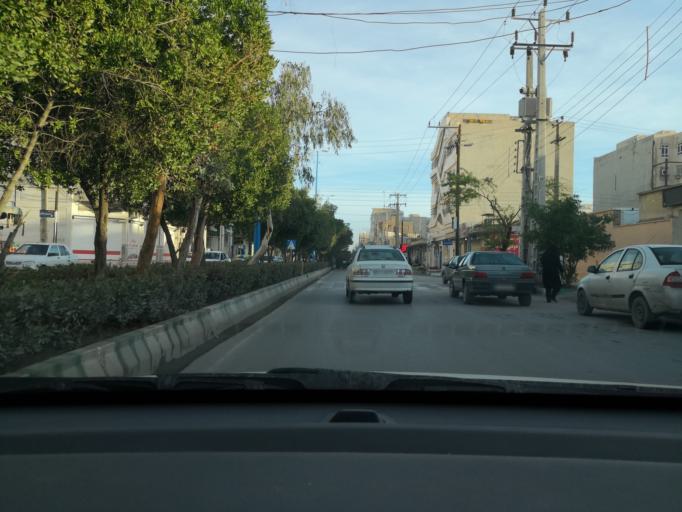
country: IR
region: Khuzestan
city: Ahvaz
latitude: 31.3519
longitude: 48.6771
